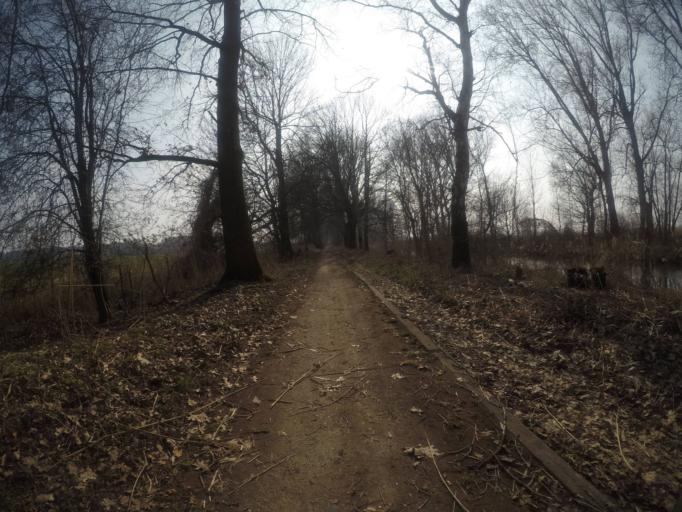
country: DE
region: Brandenburg
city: Mittenwalde
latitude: 52.2766
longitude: 13.5639
